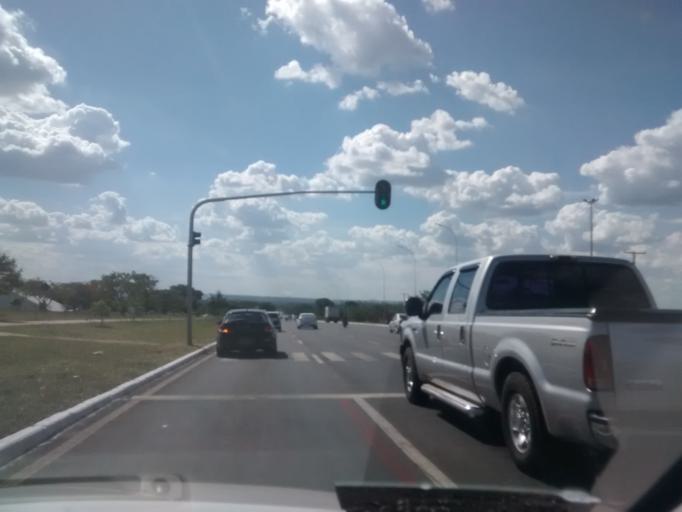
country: BR
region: Federal District
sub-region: Brasilia
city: Brasilia
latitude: -15.7806
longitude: -47.9220
